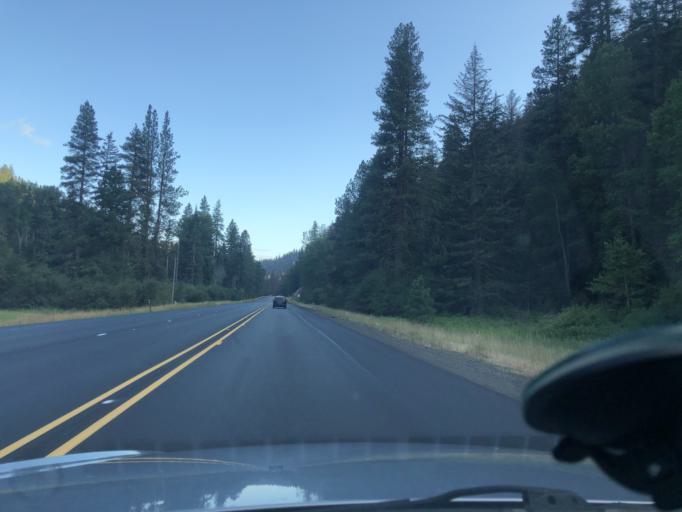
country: US
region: Washington
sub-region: Kittitas County
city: Cle Elum
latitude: 47.2724
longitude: -120.6982
